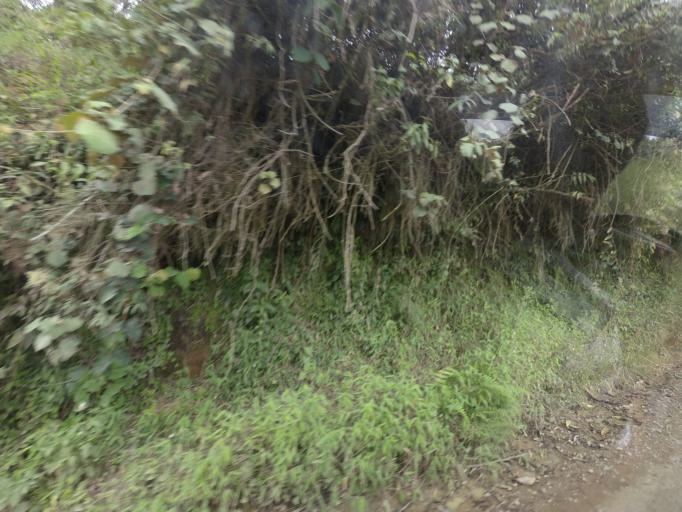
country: CO
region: Huila
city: San Agustin
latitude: 1.9303
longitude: -76.3003
